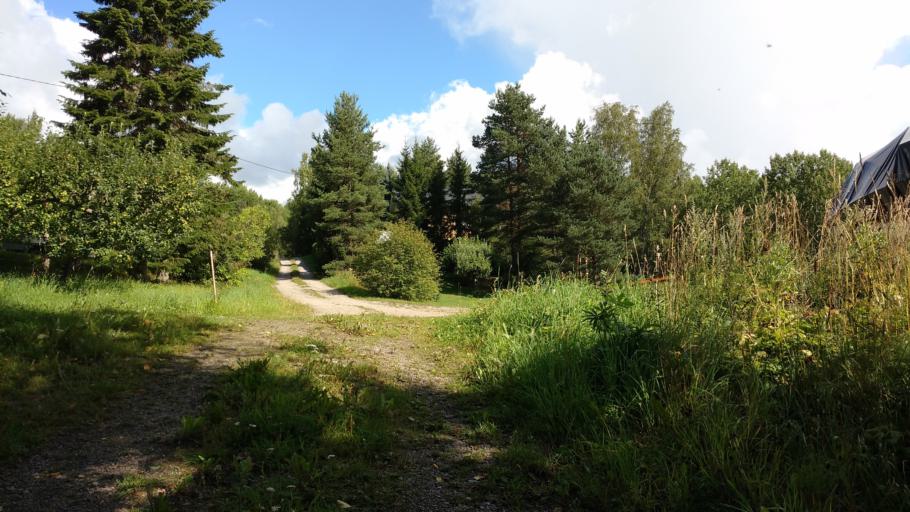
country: FI
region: Varsinais-Suomi
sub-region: Salo
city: Salo
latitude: 60.3534
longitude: 23.1351
